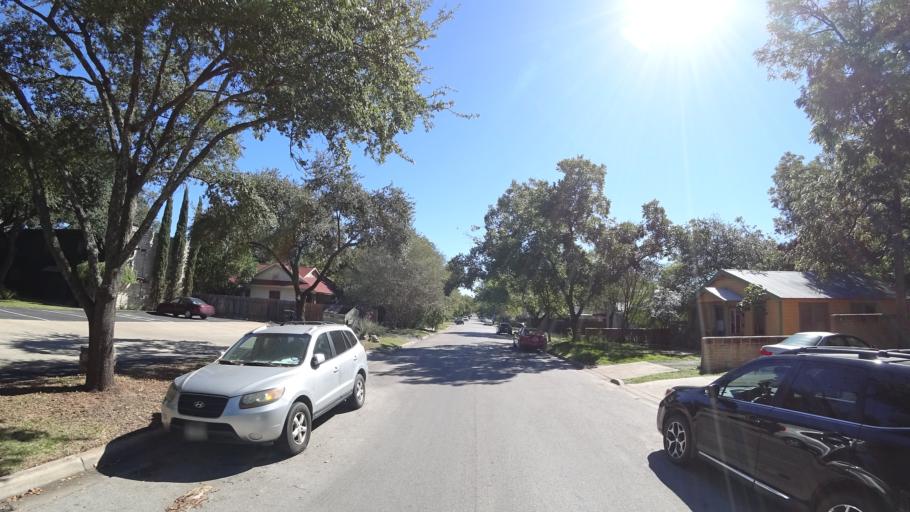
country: US
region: Texas
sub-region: Travis County
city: Austin
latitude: 30.3211
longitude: -97.7270
